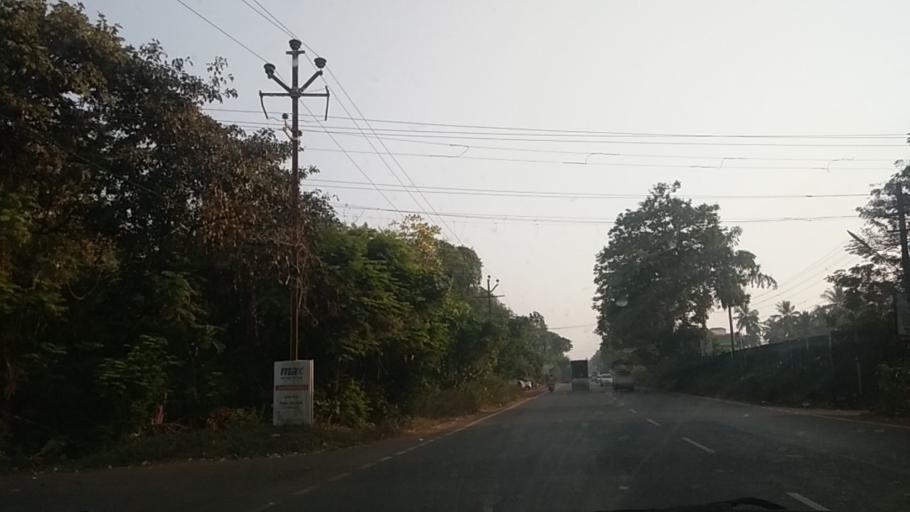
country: IN
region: Goa
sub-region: North Goa
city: Serula
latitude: 15.5400
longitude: 73.8220
